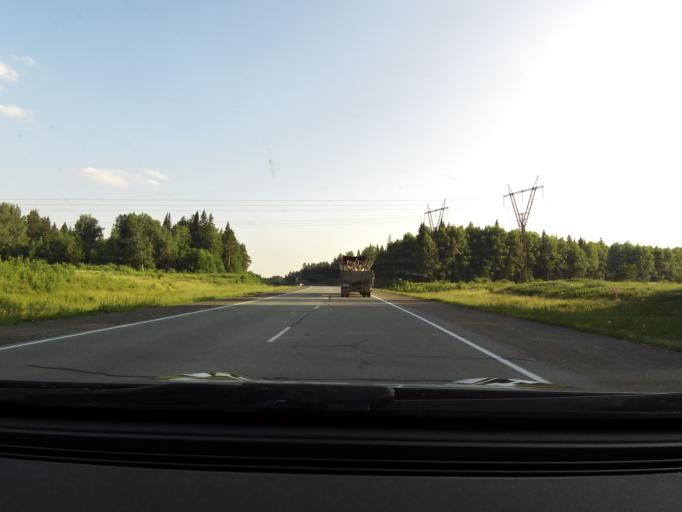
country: RU
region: Sverdlovsk
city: Druzhinino
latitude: 56.7818
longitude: 59.4541
